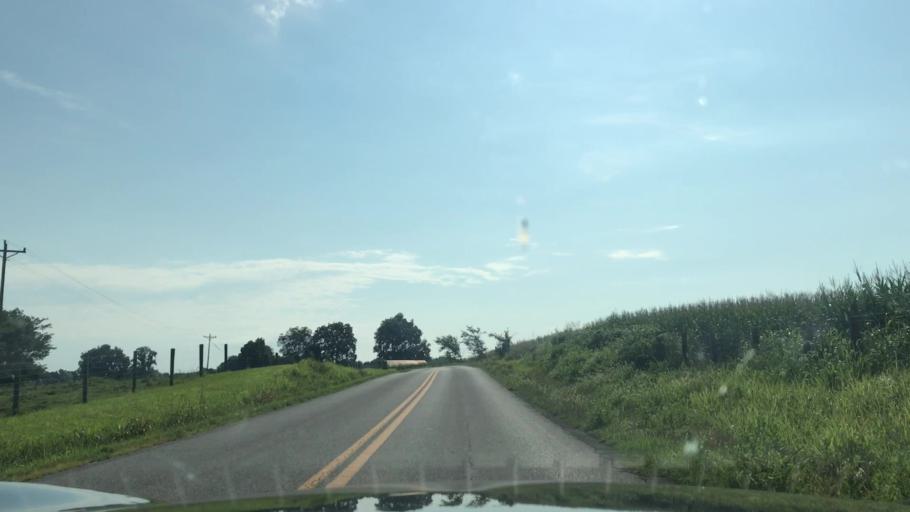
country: US
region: Kentucky
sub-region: Hart County
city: Horse Cave
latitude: 37.1874
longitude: -85.7670
